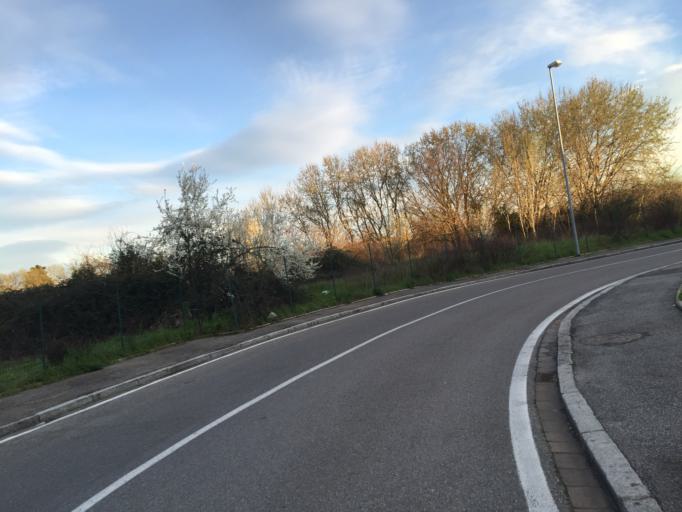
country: IT
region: Tuscany
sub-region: Provincia di Prato
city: Prato
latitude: 43.8841
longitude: 11.0555
